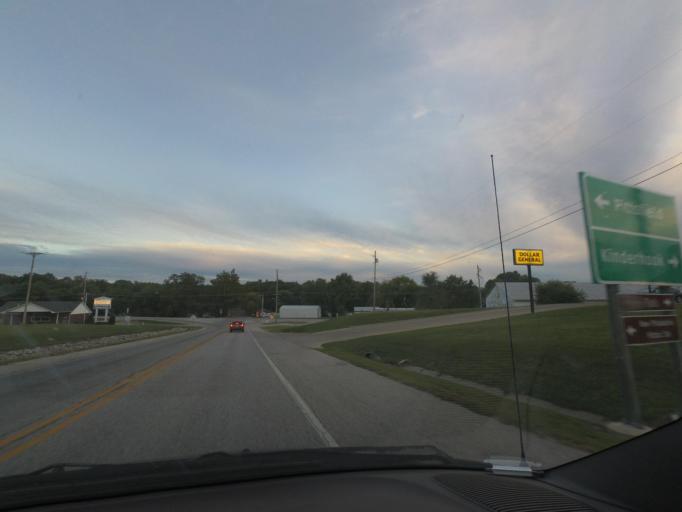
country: US
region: Illinois
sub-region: Pike County
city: Barry
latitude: 39.7009
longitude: -91.0393
